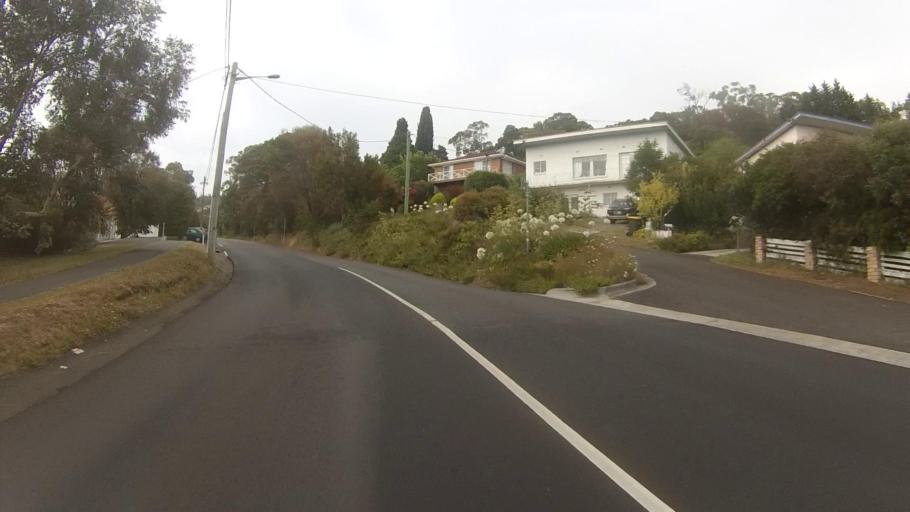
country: AU
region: Tasmania
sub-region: Hobart
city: Dynnyrne
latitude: -42.9065
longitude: 147.3271
